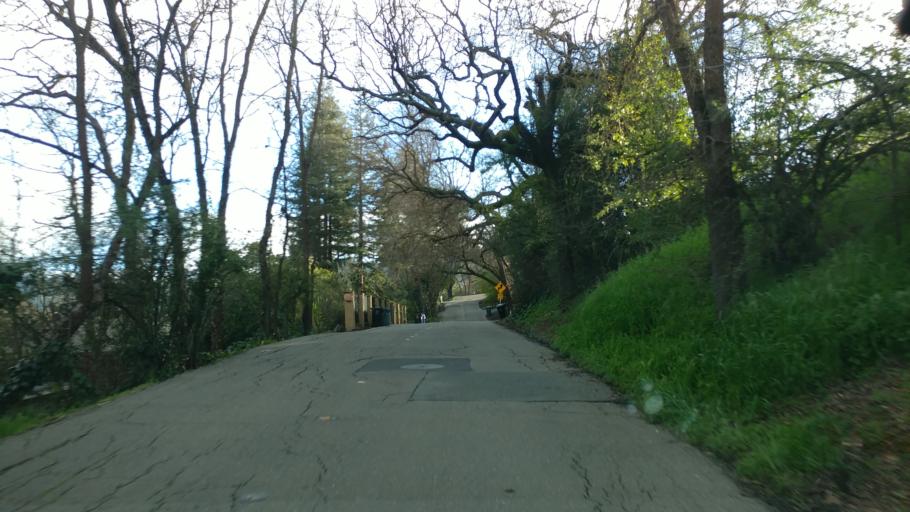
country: US
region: California
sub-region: Contra Costa County
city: Danville
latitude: 37.8326
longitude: -121.9999
